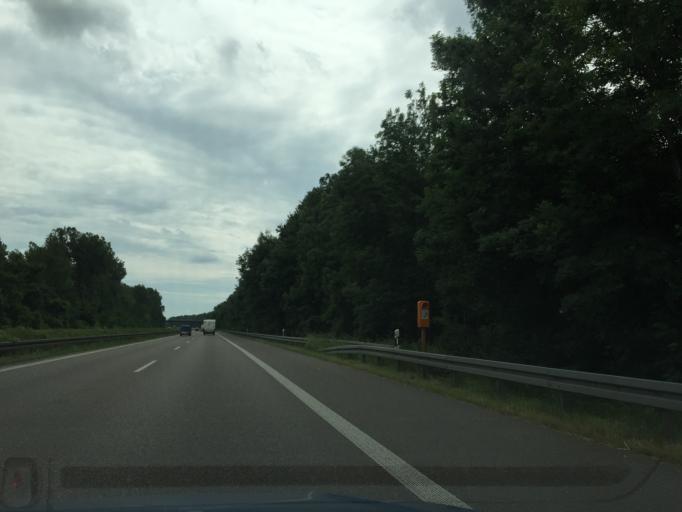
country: DE
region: Bavaria
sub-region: Swabia
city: Senden
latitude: 48.3501
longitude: 10.0157
